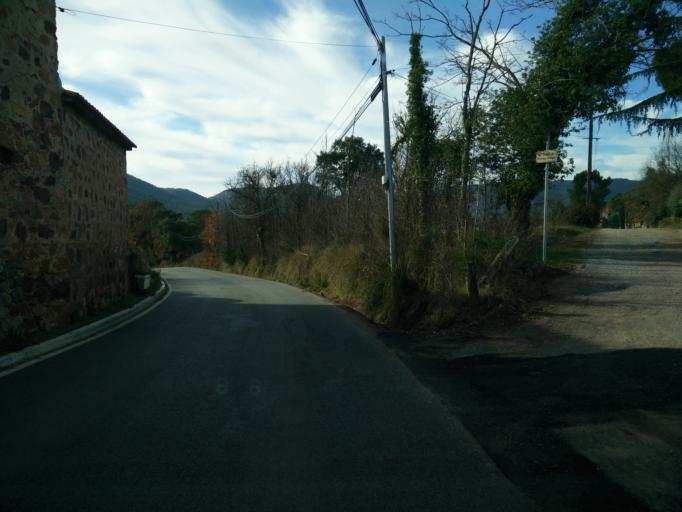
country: FR
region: Provence-Alpes-Cote d'Azur
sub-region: Departement du Var
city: Bagnols-en-Foret
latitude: 43.5392
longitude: 6.6908
